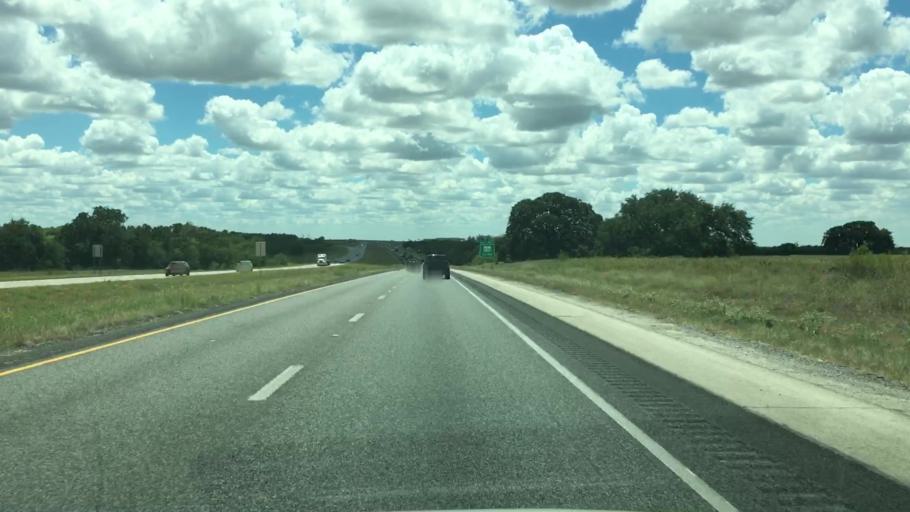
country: US
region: Texas
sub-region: Atascosa County
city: Poteet
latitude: 29.1184
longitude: -98.4318
